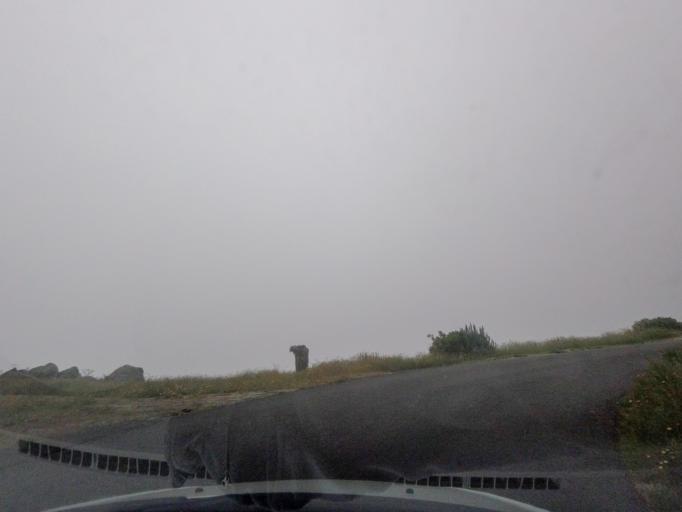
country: PT
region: Madeira
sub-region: Funchal
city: Nossa Senhora do Monte
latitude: 32.7006
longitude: -16.9110
